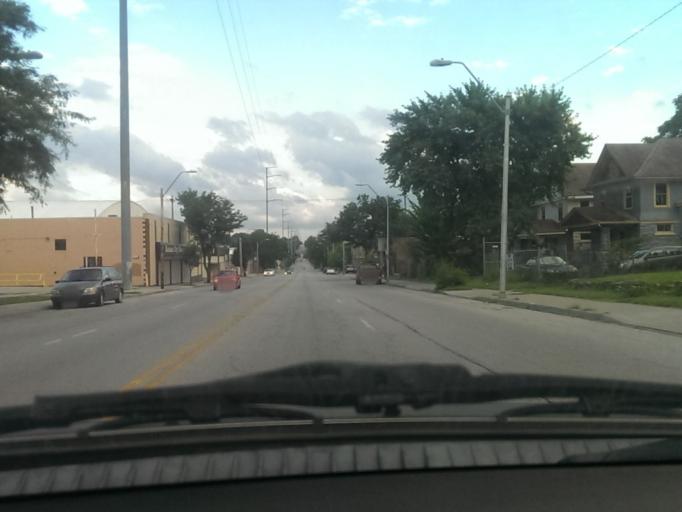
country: US
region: Kansas
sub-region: Johnson County
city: Westwood
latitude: 39.0463
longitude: -94.5727
